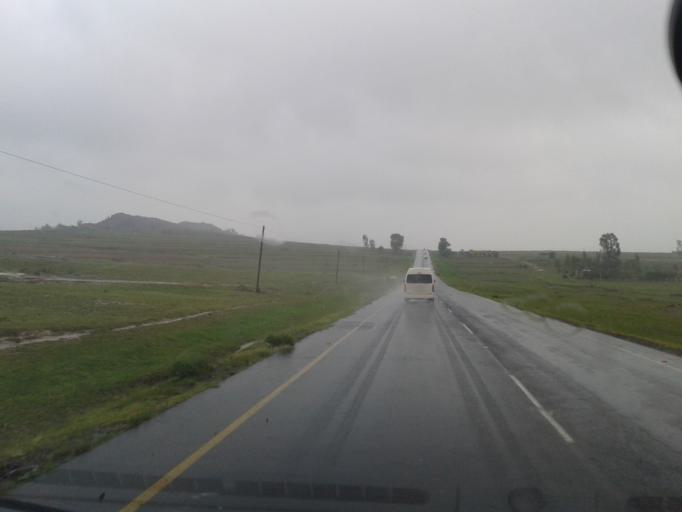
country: LS
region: Mafeteng
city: Mafeteng
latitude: -29.6735
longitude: 27.4492
